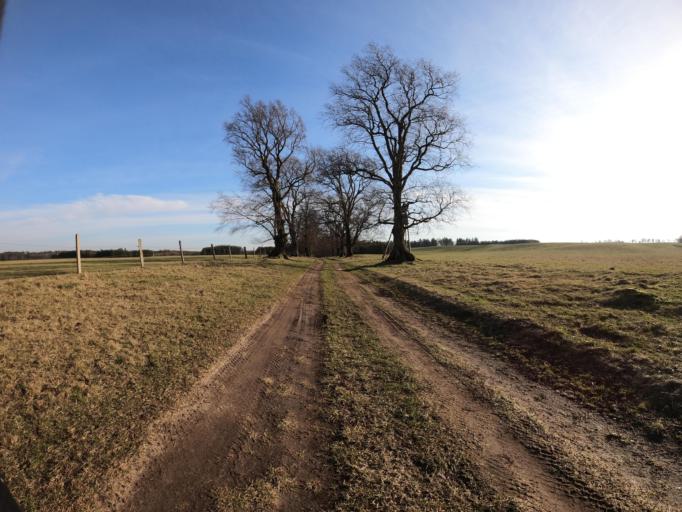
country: PL
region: West Pomeranian Voivodeship
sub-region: Powiat koszalinski
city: Polanow
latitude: 54.1956
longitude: 16.6593
